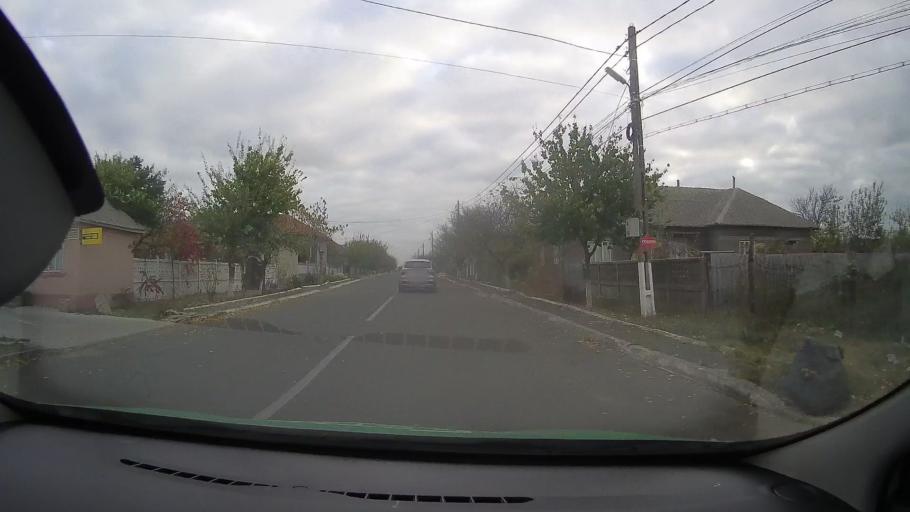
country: RO
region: Tulcea
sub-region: Comuna Jurilovca
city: Jurilovca
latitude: 44.7596
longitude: 28.8765
